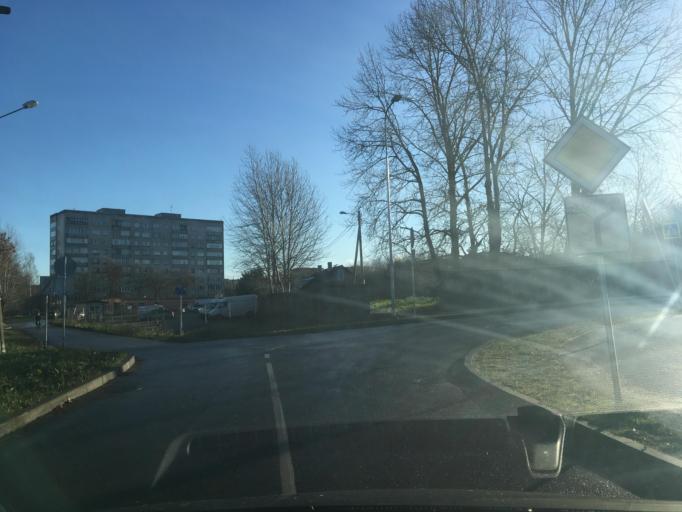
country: EE
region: Ida-Virumaa
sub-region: Narva linn
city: Narva
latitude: 59.3839
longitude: 28.1714
